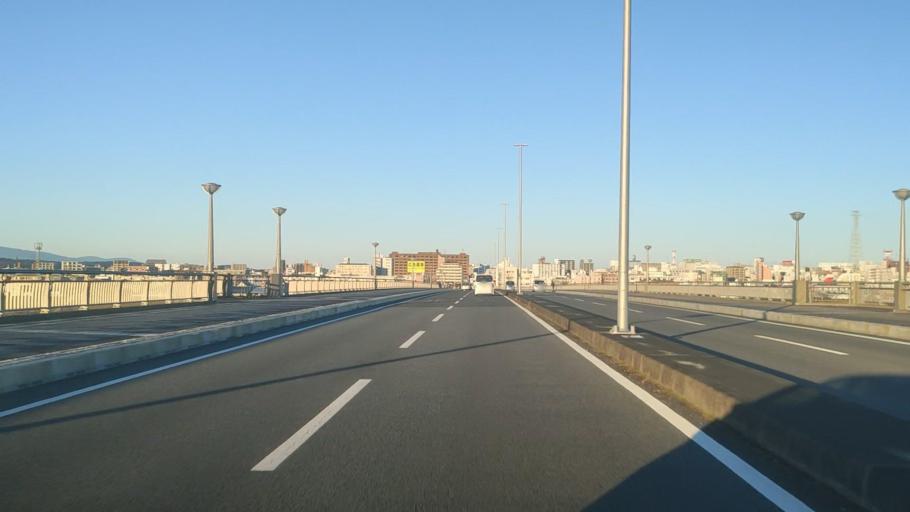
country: JP
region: Miyazaki
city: Miyazaki-shi
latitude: 31.9074
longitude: 131.4107
